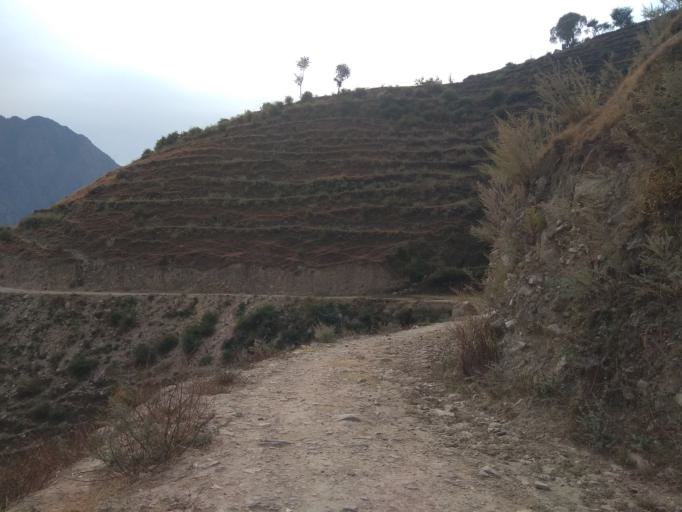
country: NP
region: Mid Western
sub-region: Bheri Zone
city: Dailekh
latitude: 29.2485
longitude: 81.6699
